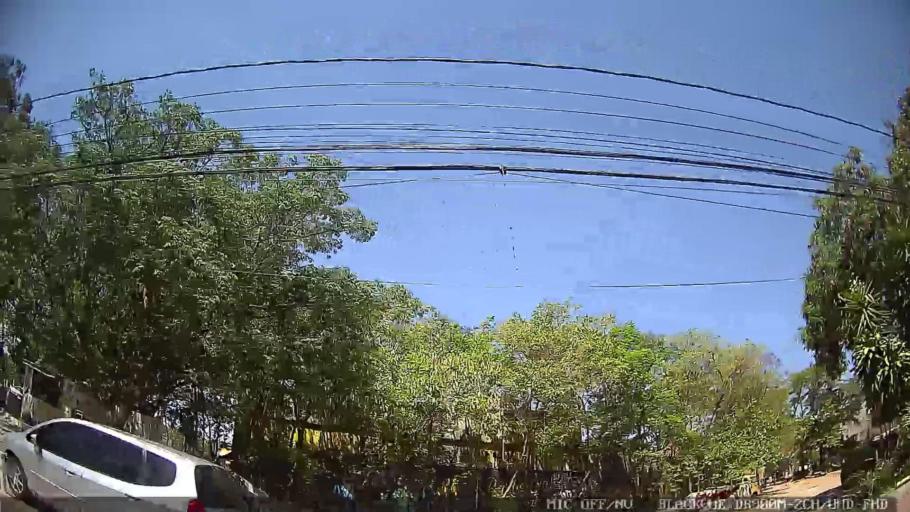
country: BR
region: Sao Paulo
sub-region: Sao Caetano Do Sul
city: Sao Caetano do Sul
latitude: -23.5855
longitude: -46.5257
